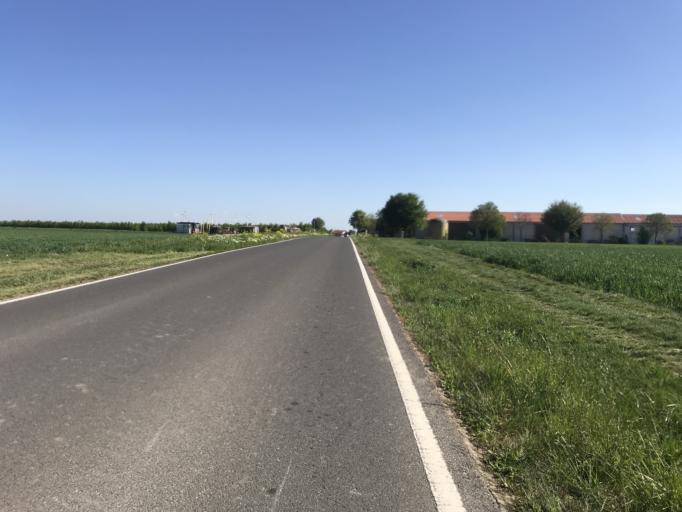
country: DE
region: Rheinland-Pfalz
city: Zornheim
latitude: 49.8799
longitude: 8.2181
